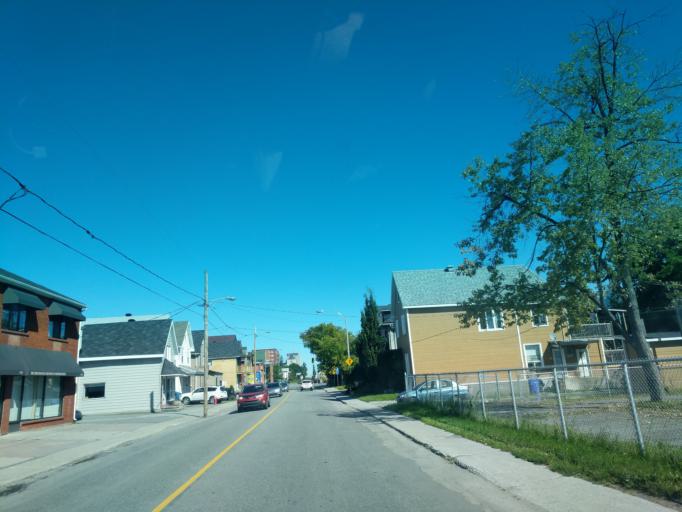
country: CA
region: Ontario
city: Ottawa
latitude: 45.4300
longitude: -75.7334
